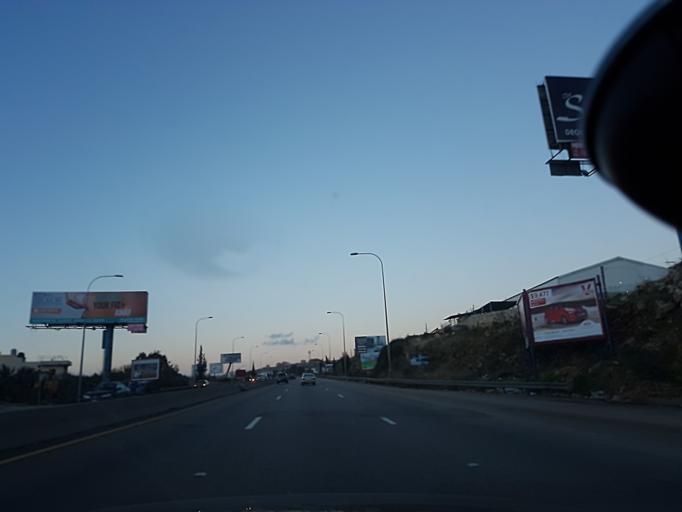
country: LB
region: Liban-Sud
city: Sidon
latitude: 33.6604
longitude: 35.4259
